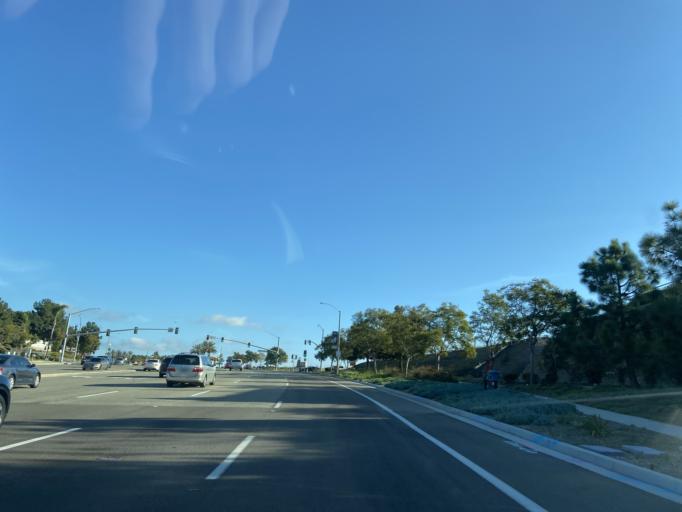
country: US
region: California
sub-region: San Diego County
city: Bonita
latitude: 32.6294
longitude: -116.9684
